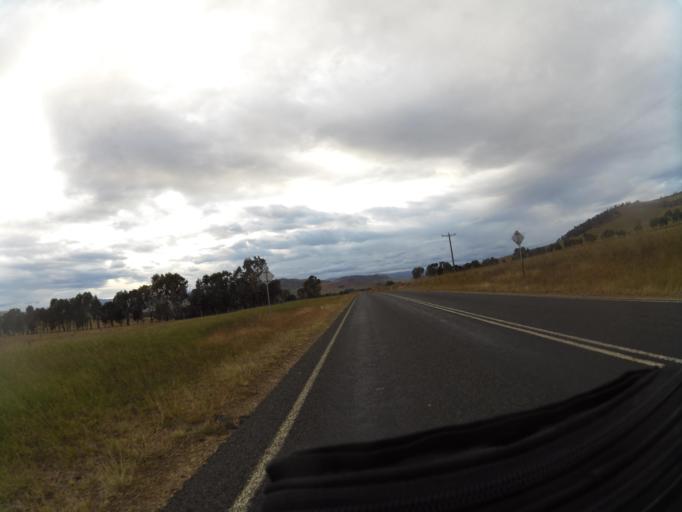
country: AU
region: New South Wales
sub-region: Greater Hume Shire
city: Holbrook
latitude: -36.0725
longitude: 147.9652
